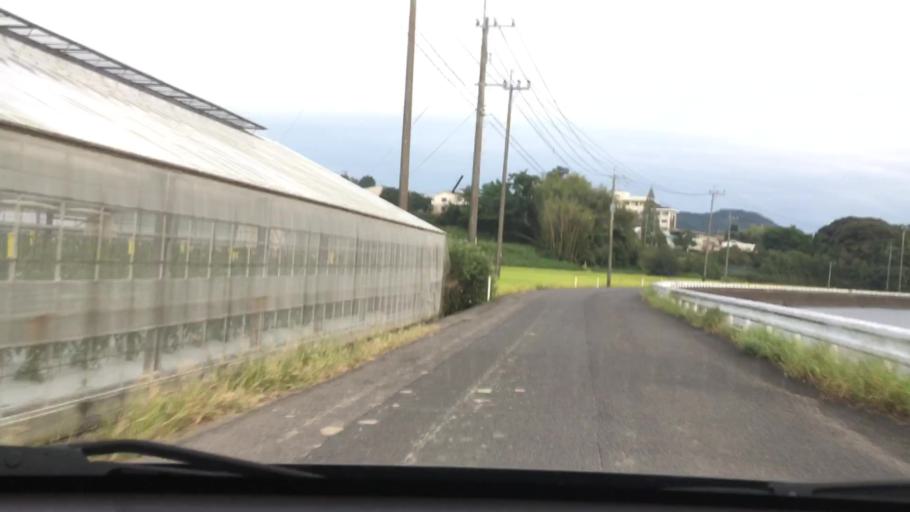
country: JP
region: Nagasaki
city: Sasebo
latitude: 32.9911
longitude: 129.7723
